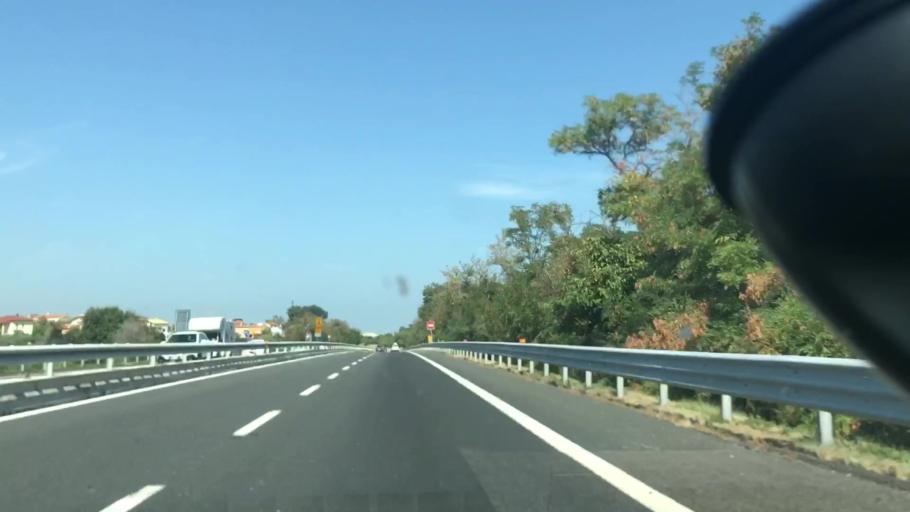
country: IT
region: Abruzzo
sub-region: Provincia di Chieti
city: Vasto
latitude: 42.0993
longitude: 14.6972
